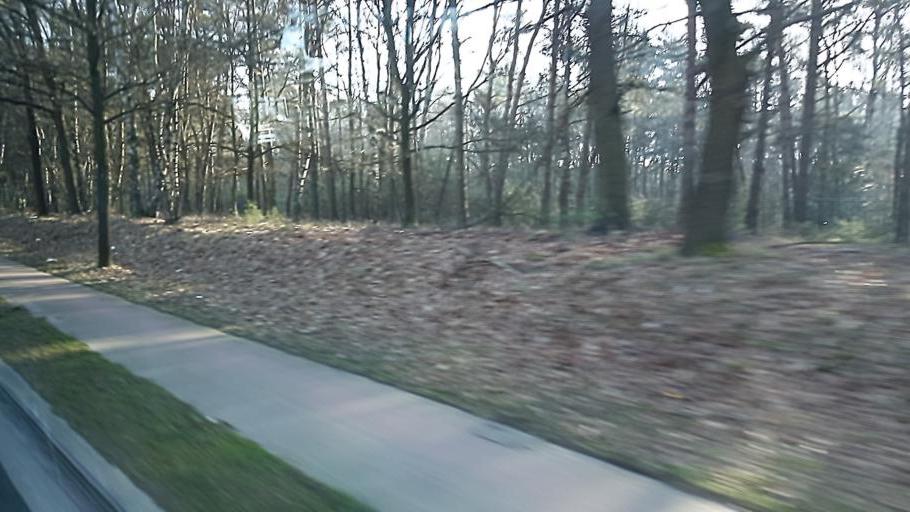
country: BE
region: Flanders
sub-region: Provincie Limburg
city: Genk
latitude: 51.0027
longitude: 5.4769
